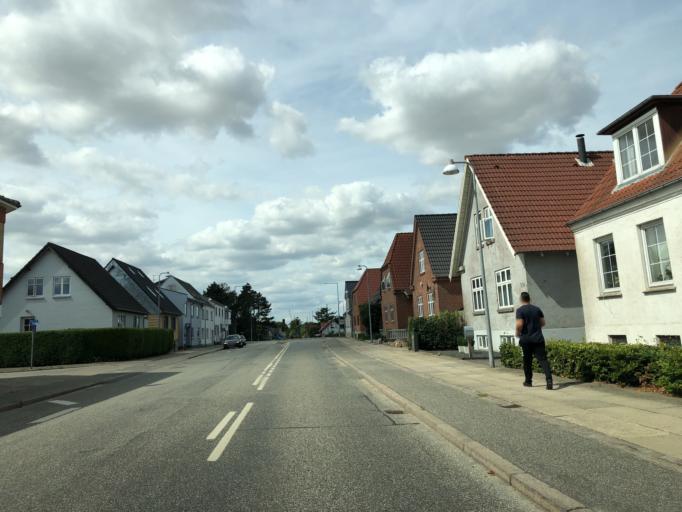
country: DK
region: Central Jutland
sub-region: Herning Kommune
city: Herning
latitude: 56.1357
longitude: 8.9521
